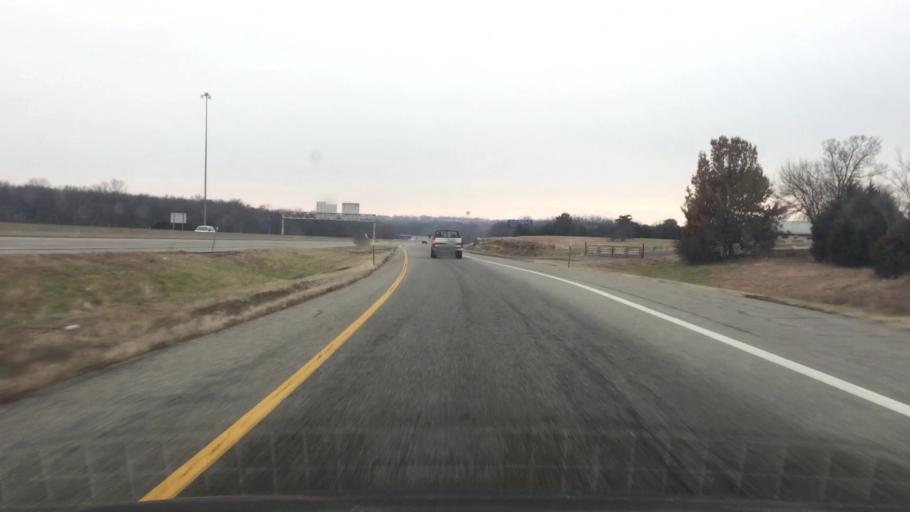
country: US
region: Kansas
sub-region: Shawnee County
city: Topeka
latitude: 39.0279
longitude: -95.6217
